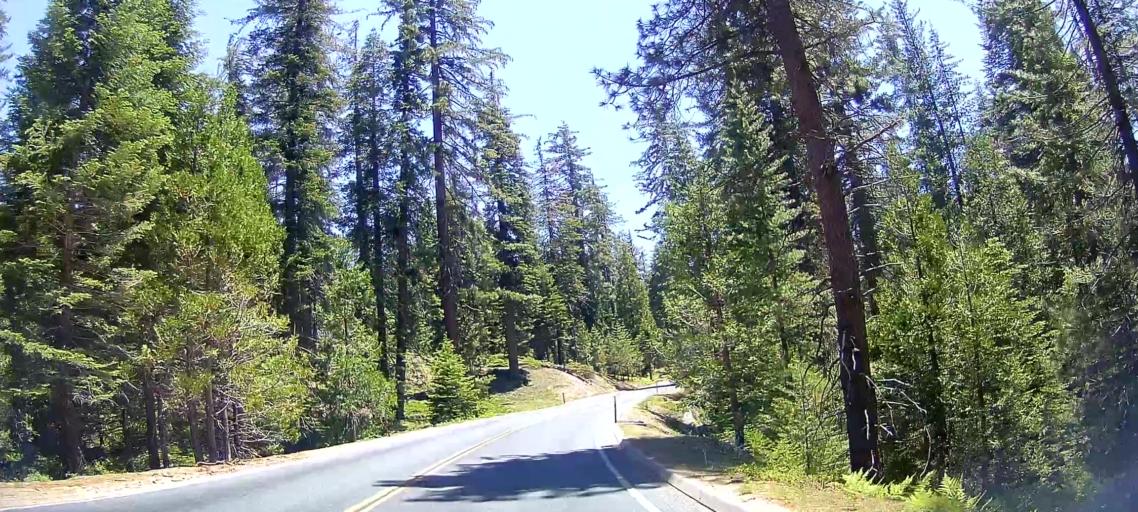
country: US
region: California
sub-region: Fresno County
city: Squaw Valley
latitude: 36.7315
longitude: -118.9611
